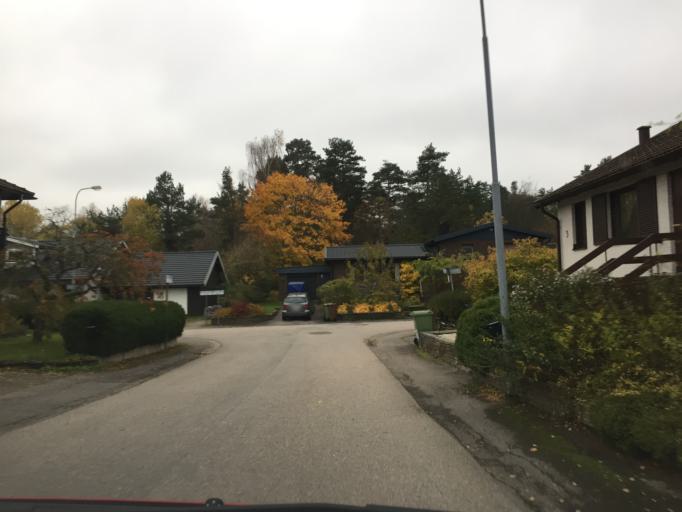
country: SE
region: Vaestra Goetaland
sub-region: Trollhattan
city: Trollhattan
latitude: 58.2656
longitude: 12.2848
